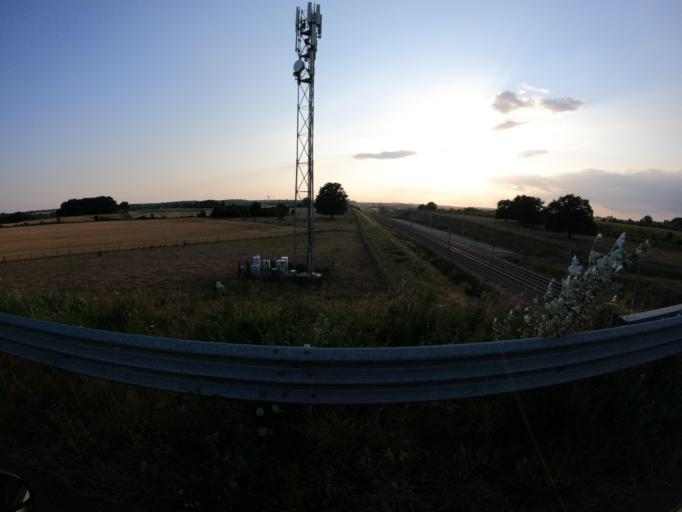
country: FR
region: Pays de la Loire
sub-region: Departement de la Sarthe
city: Brulon
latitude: 47.9099
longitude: -0.2291
